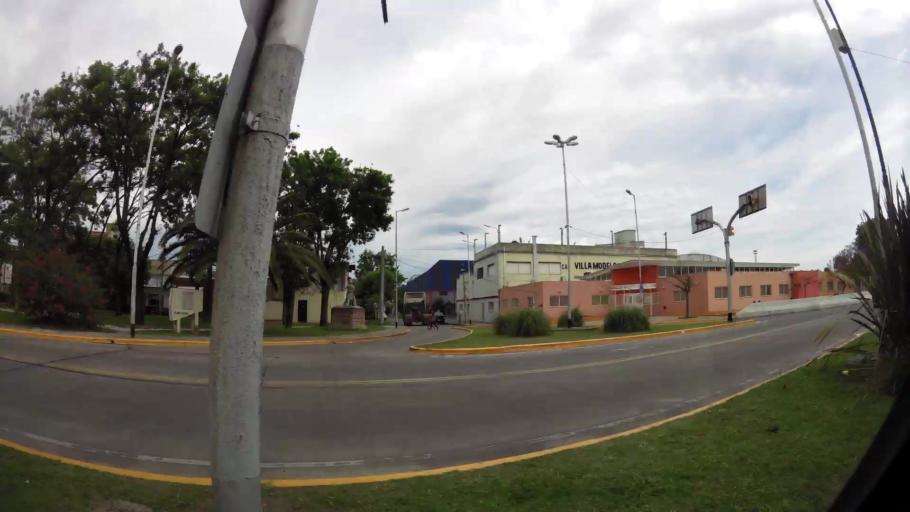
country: AR
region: Buenos Aires
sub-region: Partido de Avellaneda
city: Avellaneda
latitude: -34.6813
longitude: -58.3775
